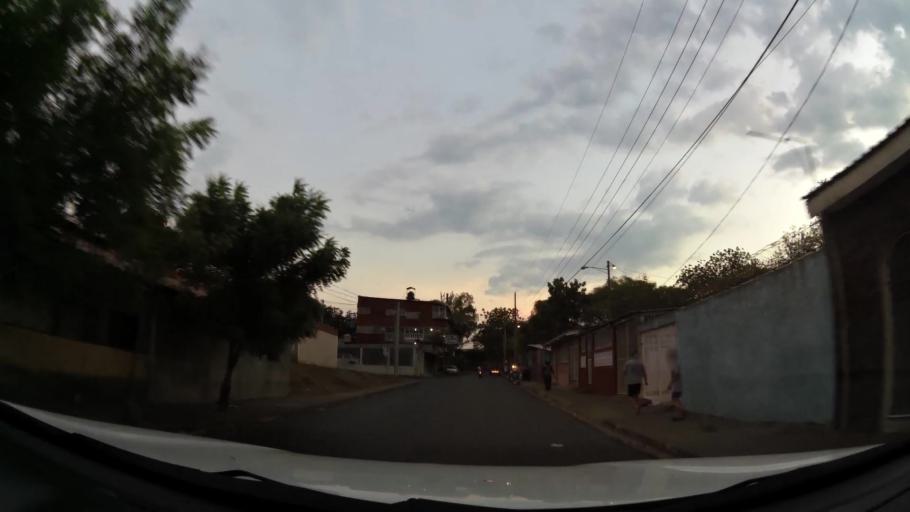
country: NI
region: Managua
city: Managua
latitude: 12.1267
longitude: -86.2406
